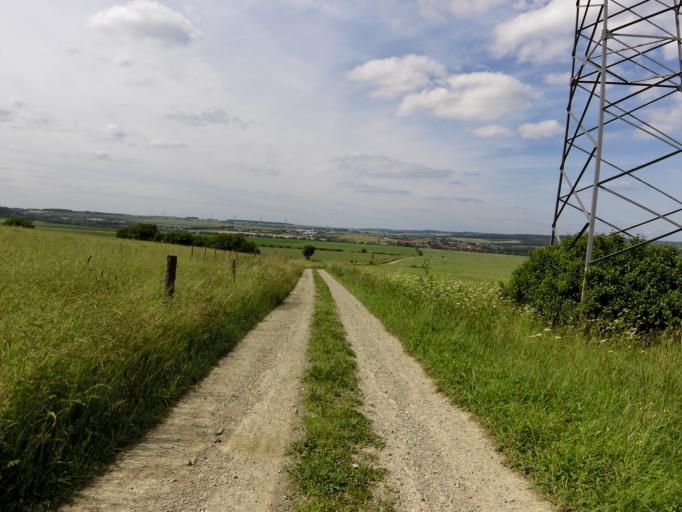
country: DE
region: Thuringia
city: Seebach
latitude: 50.9716
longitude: 10.4102
